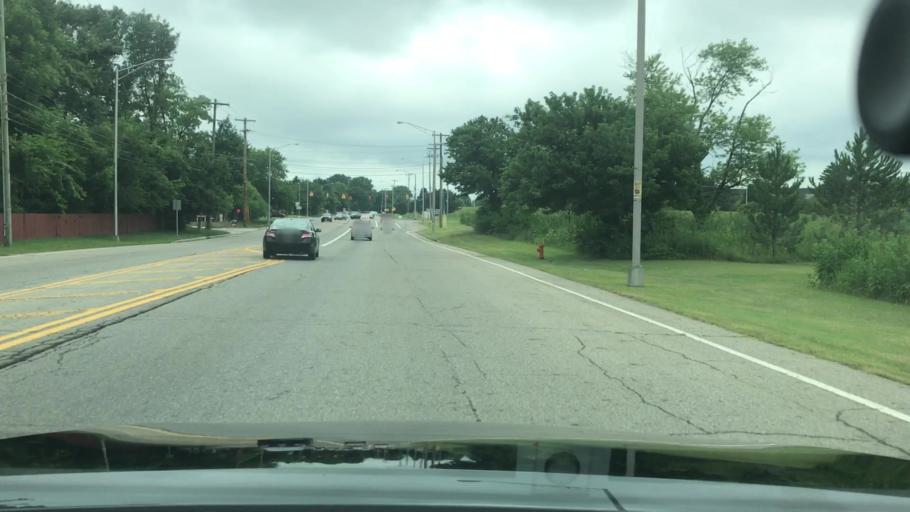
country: US
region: Ohio
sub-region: Franklin County
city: Lincoln Village
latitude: 39.9883
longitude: -83.1053
